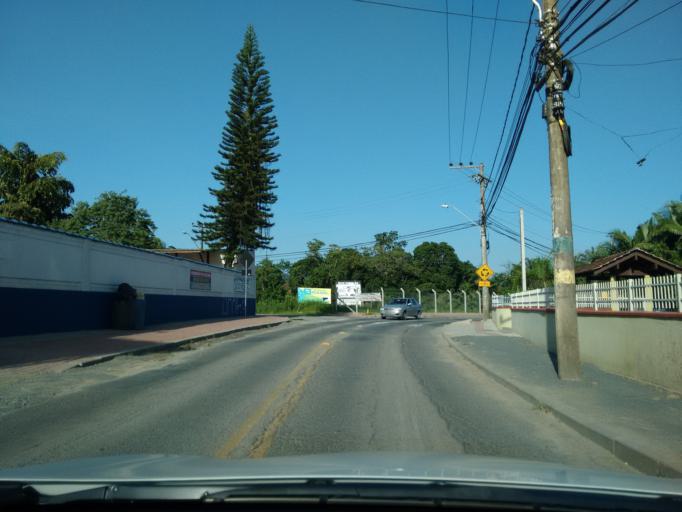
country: BR
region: Santa Catarina
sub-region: Blumenau
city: Blumenau
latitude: -26.8490
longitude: -49.0818
